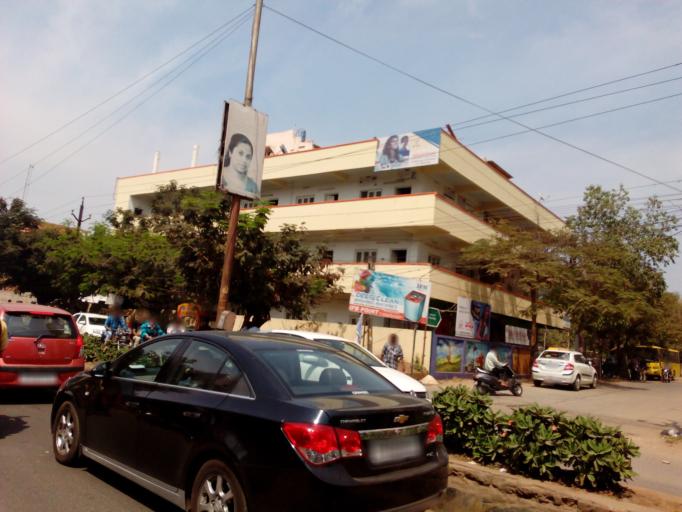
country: IN
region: Andhra Pradesh
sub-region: Krishna
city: Yanamalakuduru
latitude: 16.5016
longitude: 80.6539
